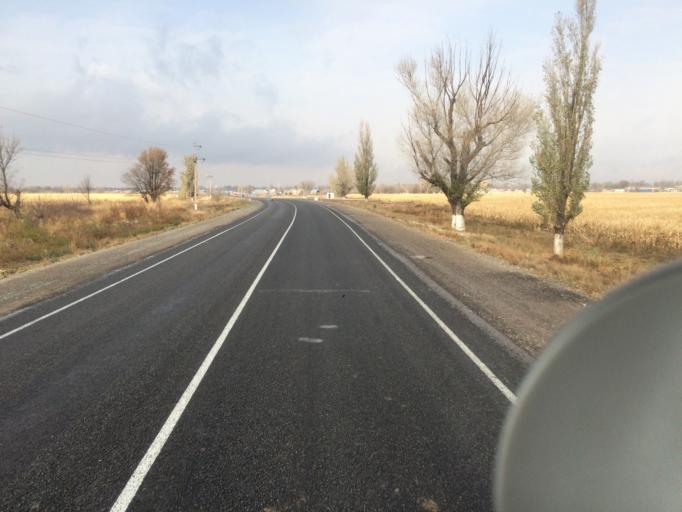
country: KZ
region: Zhambyl
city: Georgiyevka
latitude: 43.1543
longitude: 74.6023
